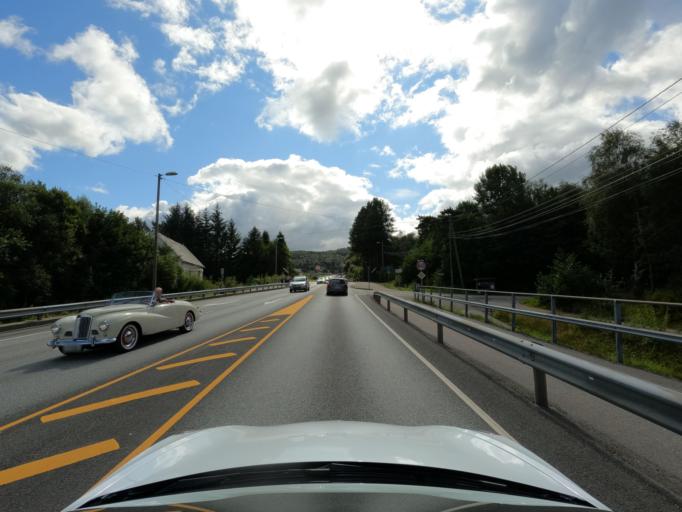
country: NO
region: Hordaland
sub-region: Bergen
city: Hylkje
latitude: 60.4899
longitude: 5.3768
